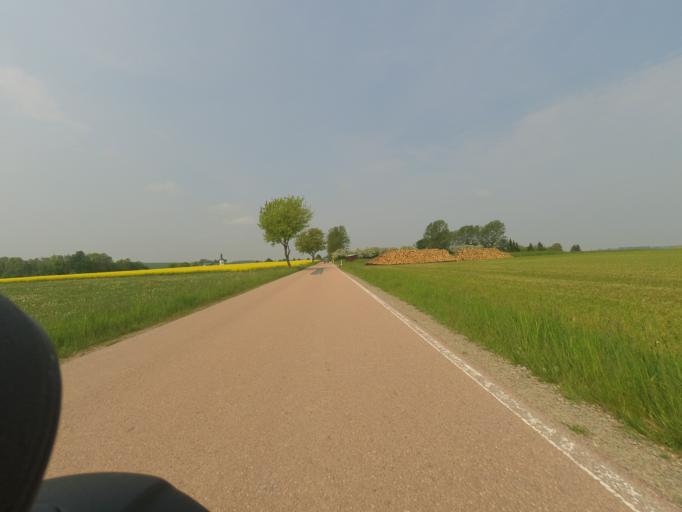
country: DE
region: Saxony
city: Pretzschendorf
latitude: 50.8733
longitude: 13.5339
